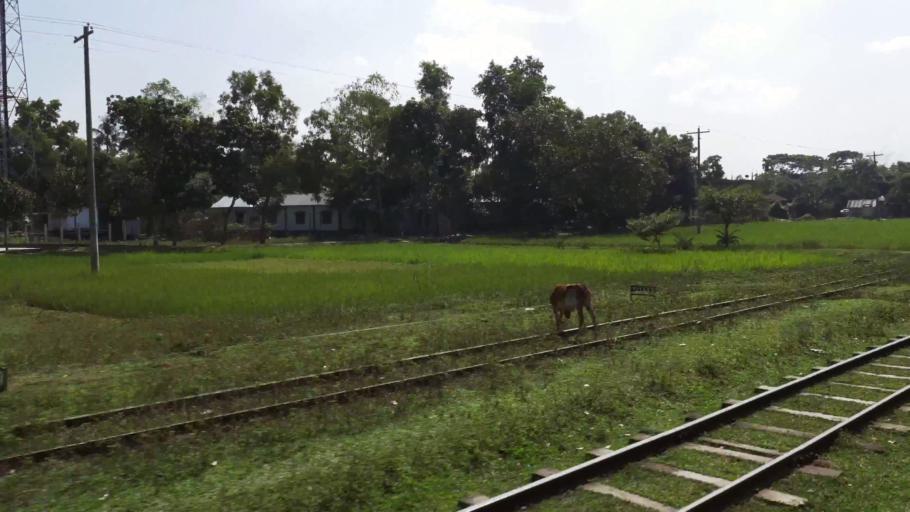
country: BD
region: Dhaka
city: Gafargaon
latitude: 24.2333
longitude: 90.4899
